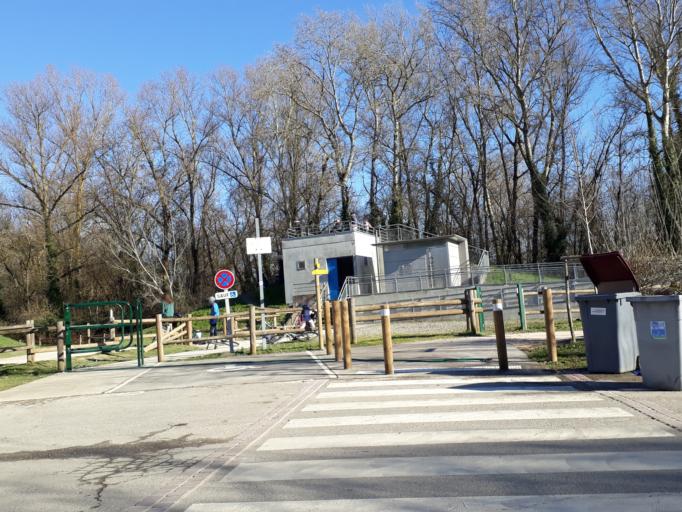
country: FR
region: Midi-Pyrenees
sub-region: Departement de la Haute-Garonne
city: Fenouillet
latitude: 43.6641
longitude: 1.3932
